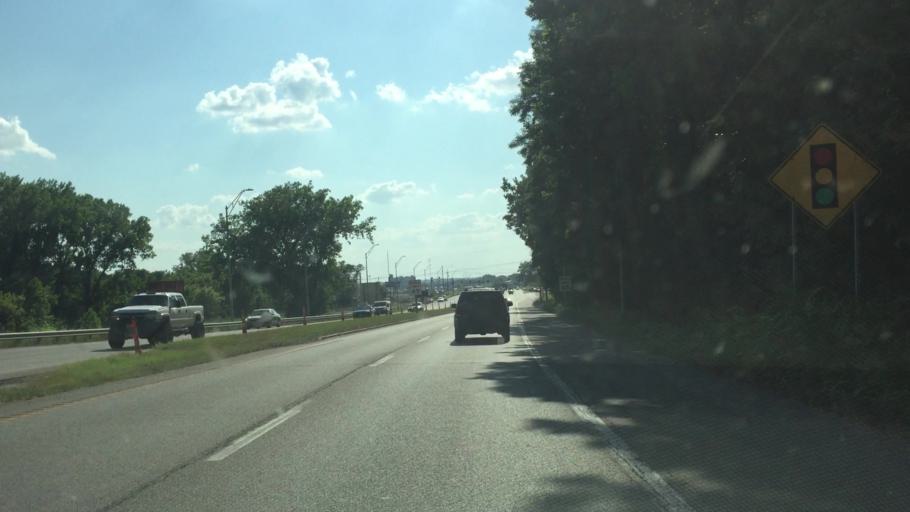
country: US
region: Missouri
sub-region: Clay County
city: North Kansas City
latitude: 39.1474
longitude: -94.5440
